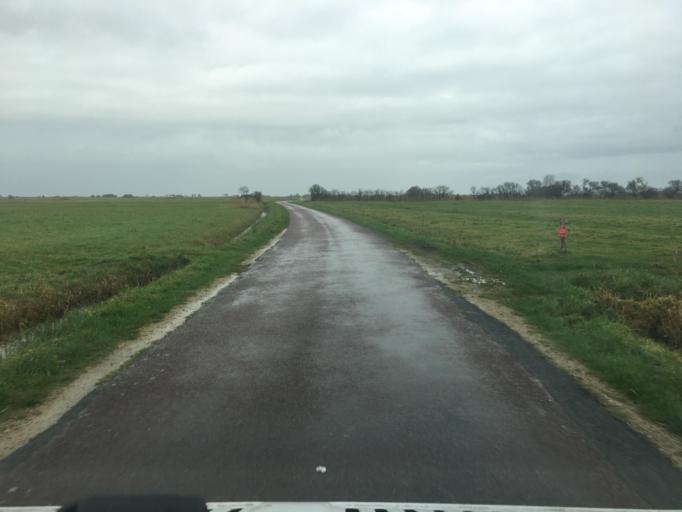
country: FR
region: Lower Normandy
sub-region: Departement de la Manche
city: Sainte-Mere-Eglise
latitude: 49.4442
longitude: -1.2423
